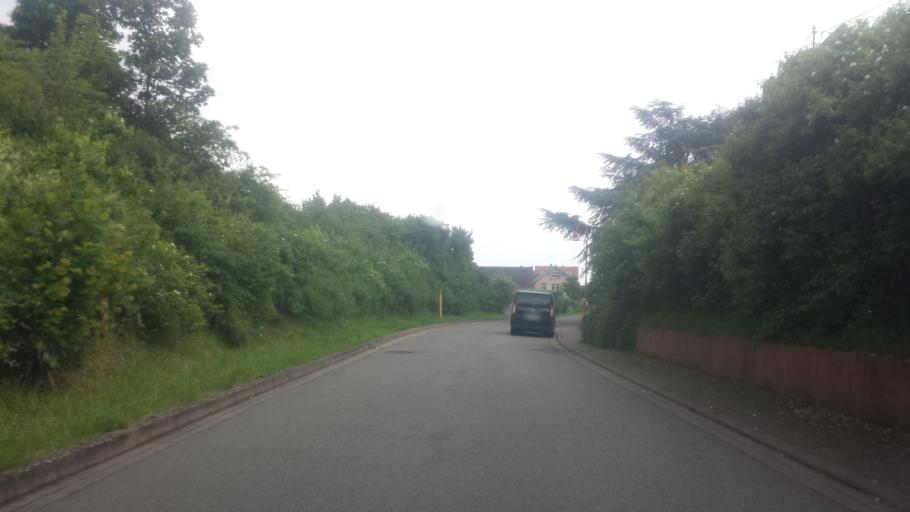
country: DE
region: Rheinland-Pfalz
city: Rhodt unter Rietburg
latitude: 49.2836
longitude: 8.1119
